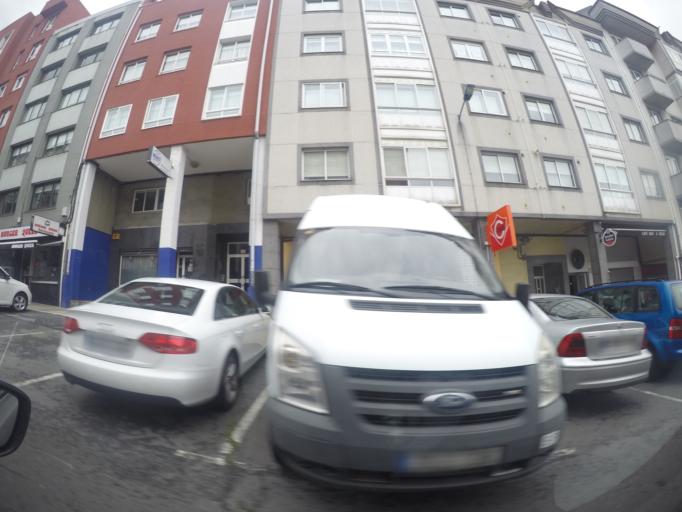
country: ES
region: Galicia
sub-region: Provincia da Coruna
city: Culleredo
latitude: 43.3106
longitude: -8.3826
